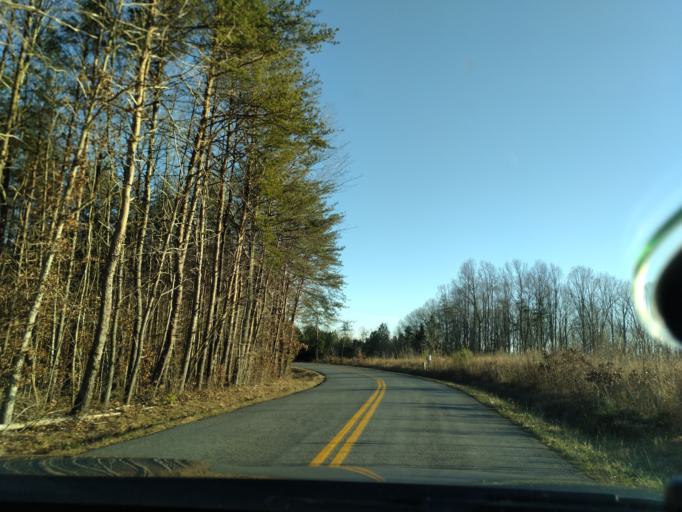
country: US
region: Virginia
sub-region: Prince Edward County
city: Hampden Sydney
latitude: 37.3232
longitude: -78.5762
